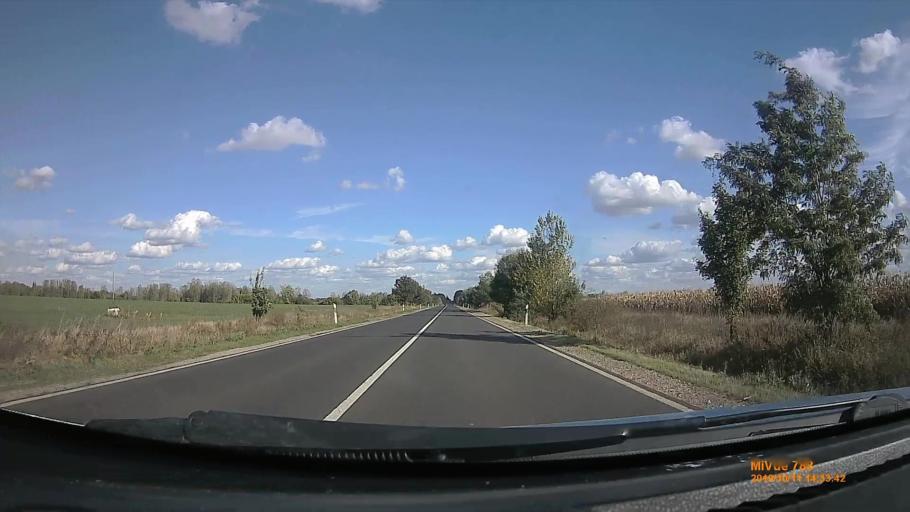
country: HU
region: Hajdu-Bihar
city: Ebes
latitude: 47.5614
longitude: 21.4613
